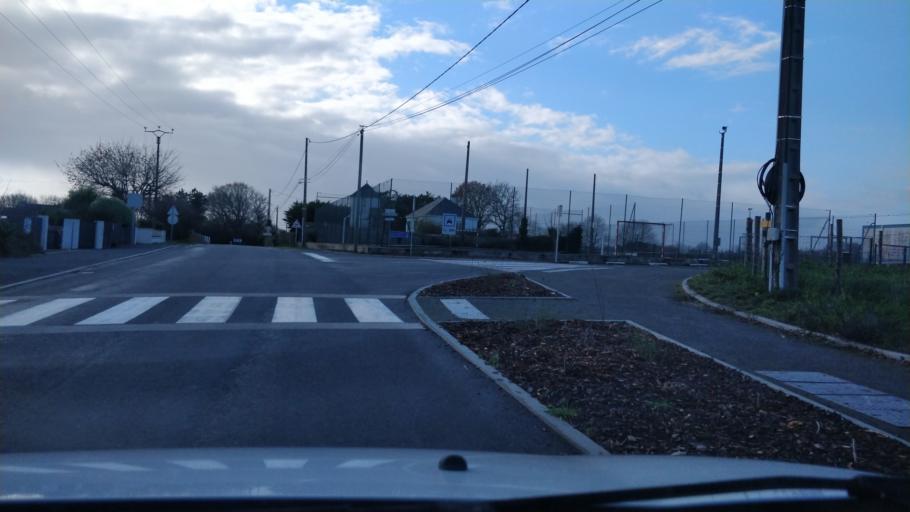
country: FR
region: Pays de la Loire
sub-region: Departement de la Loire-Atlantique
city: Asserac
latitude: 47.4219
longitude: -2.3963
